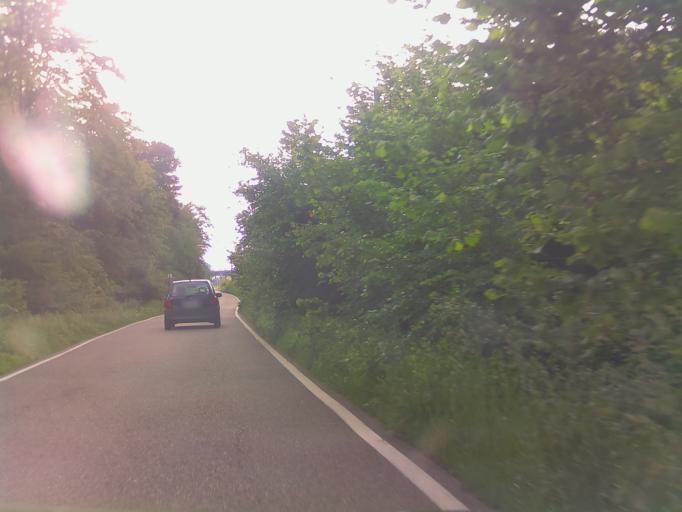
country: DE
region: Rheinland-Pfalz
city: Schifferstadt
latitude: 49.3677
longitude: 8.3836
